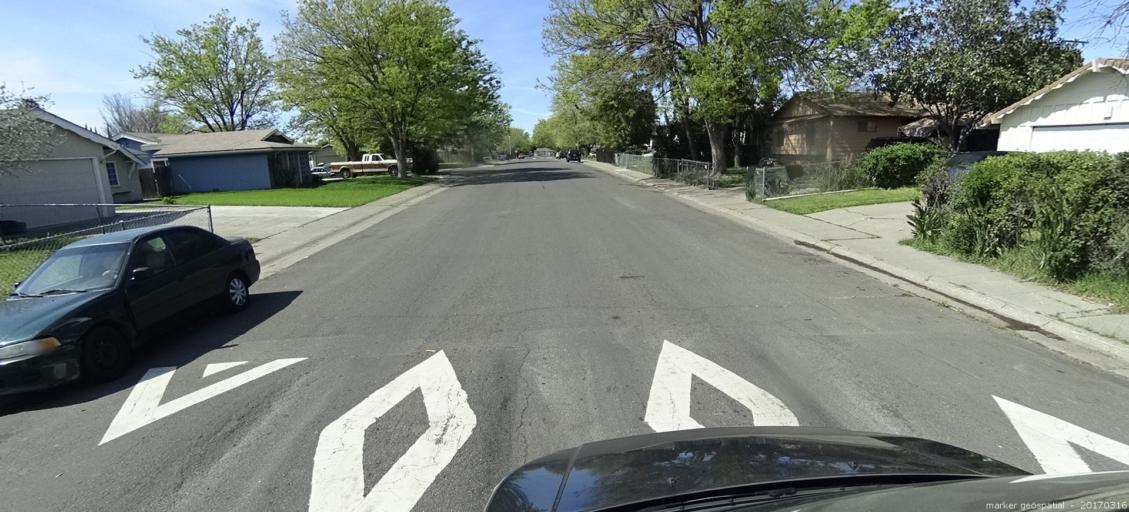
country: US
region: California
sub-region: Sacramento County
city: Parkway
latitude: 38.4788
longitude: -121.4770
